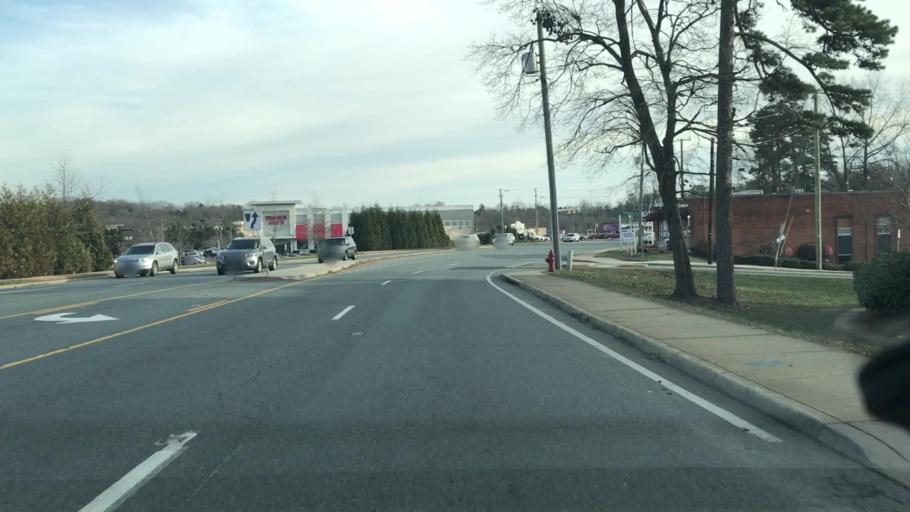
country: US
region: Virginia
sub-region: City of Charlottesville
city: Charlottesville
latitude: 38.0638
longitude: -78.4929
